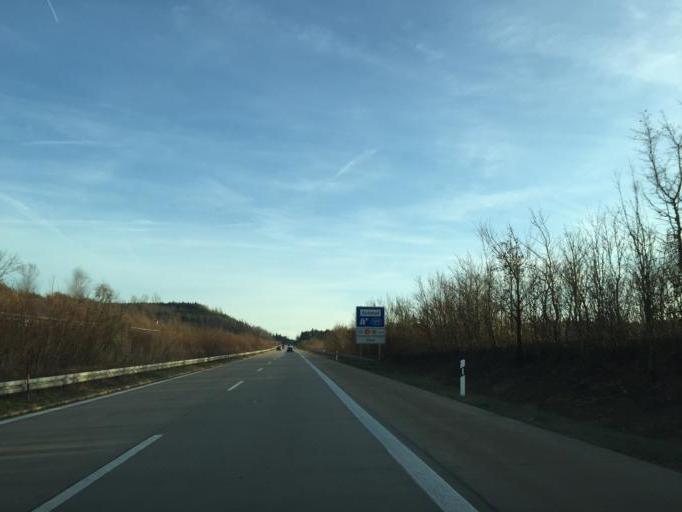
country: DE
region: Bavaria
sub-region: Regierungsbezirk Mittelfranken
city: Diebach
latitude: 49.2876
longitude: 10.2226
